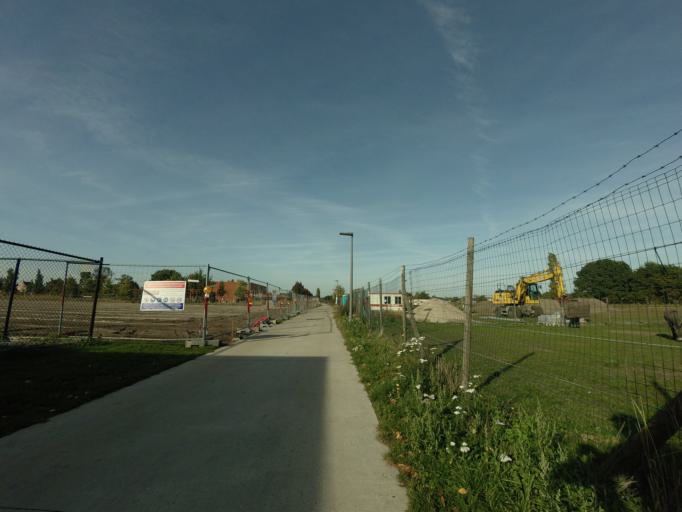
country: BE
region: Flanders
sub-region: Provincie Antwerpen
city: Stabroek
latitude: 51.3478
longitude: 4.3164
